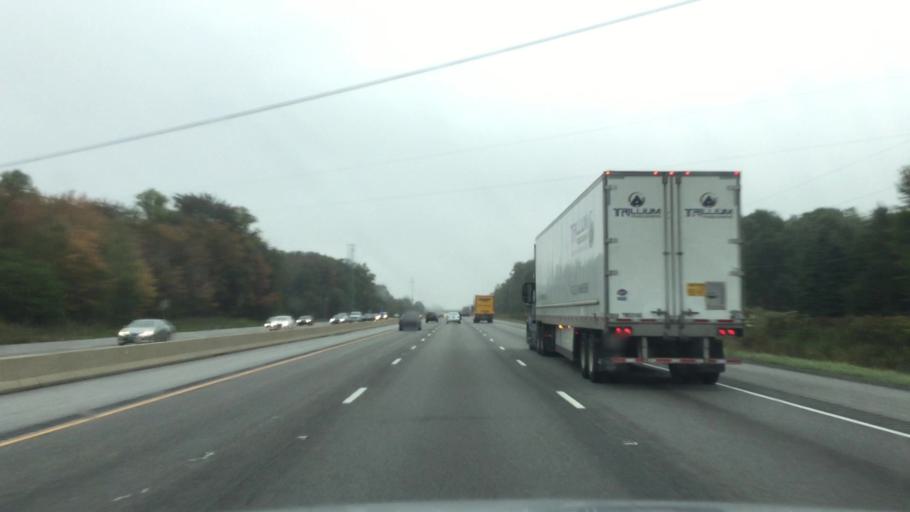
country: US
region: Indiana
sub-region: LaPorte County
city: Long Beach
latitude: 41.7311
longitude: -86.7966
